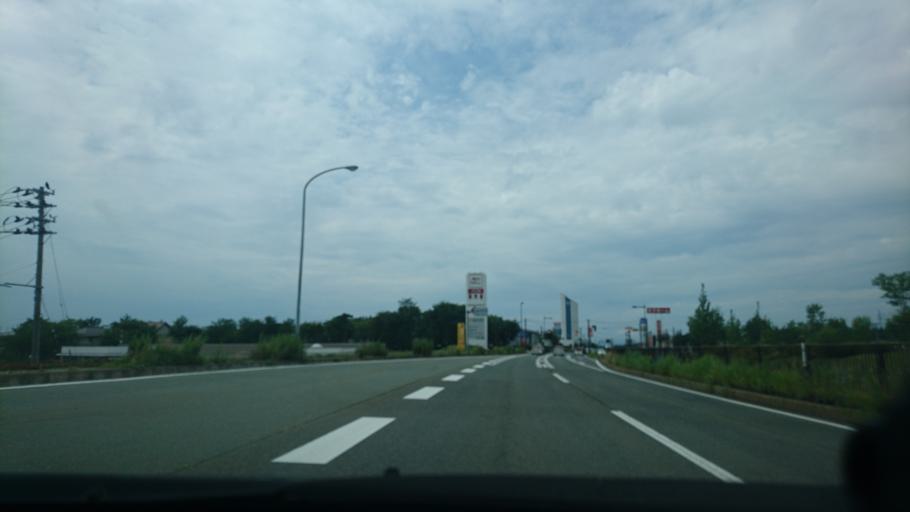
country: JP
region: Akita
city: Akita
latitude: 39.6655
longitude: 140.1704
